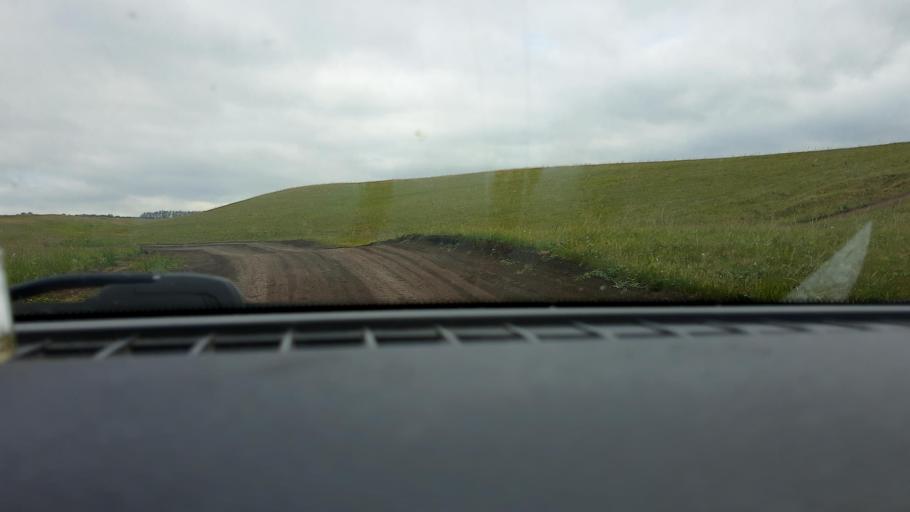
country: RU
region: Bashkortostan
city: Chishmy
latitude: 54.6860
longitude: 55.4834
